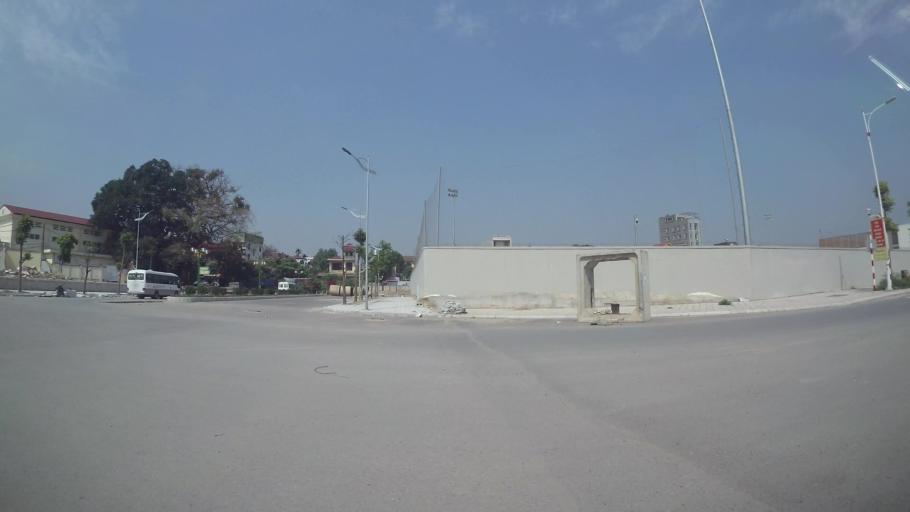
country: VN
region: Ha Noi
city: Hoan Kiem
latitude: 21.0593
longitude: 105.8697
